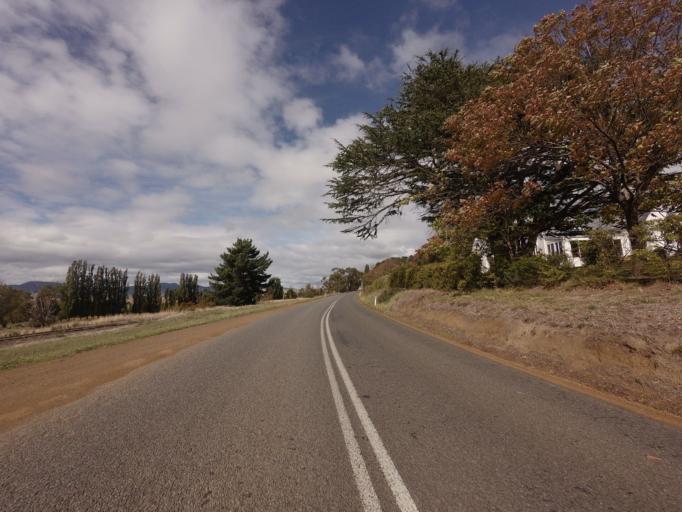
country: AU
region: Tasmania
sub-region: Derwent Valley
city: New Norfolk
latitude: -42.6835
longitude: 146.8667
